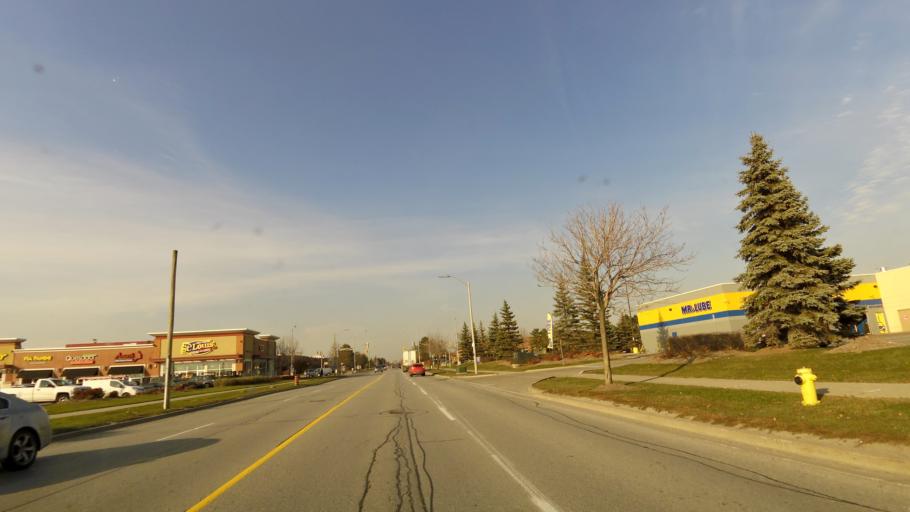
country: CA
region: Ontario
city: Concord
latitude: 43.7960
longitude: -79.5323
